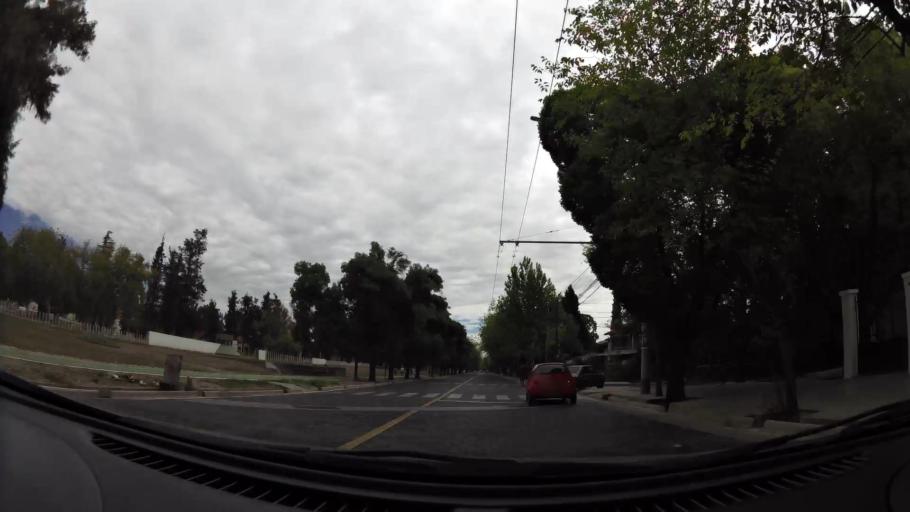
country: AR
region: Mendoza
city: Mendoza
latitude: -32.8814
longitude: -68.8602
